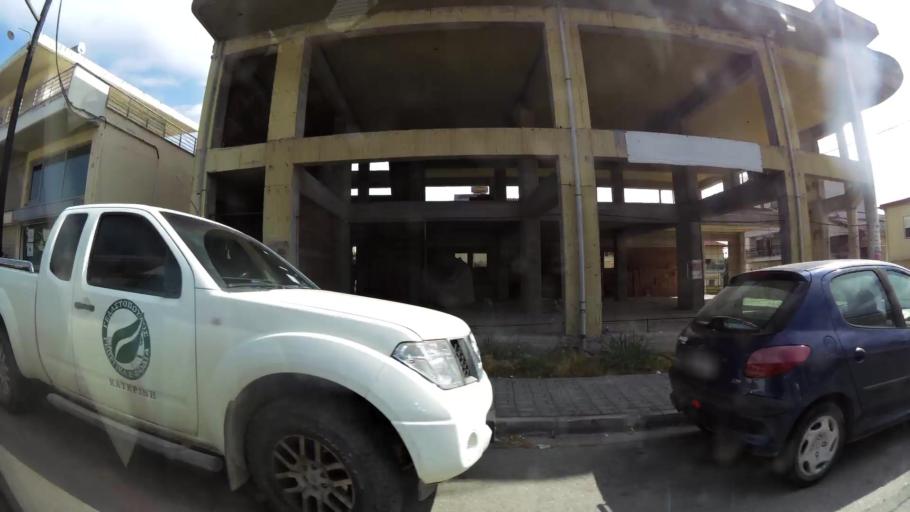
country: GR
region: Central Macedonia
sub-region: Nomos Pierias
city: Katerini
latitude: 40.2762
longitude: 22.5147
